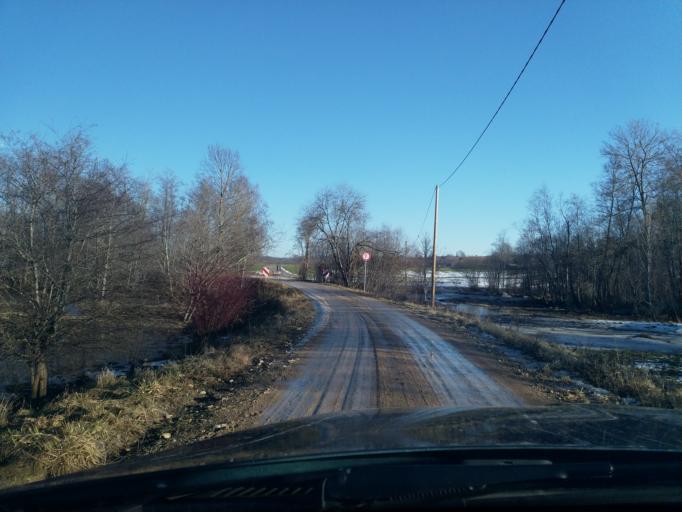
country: LV
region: Talsu Rajons
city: Sabile
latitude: 57.0141
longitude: 22.6220
